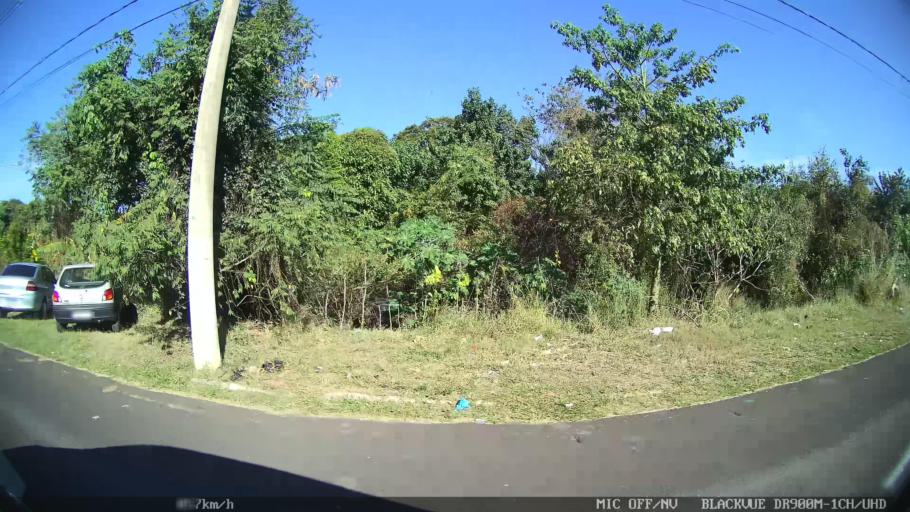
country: BR
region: Sao Paulo
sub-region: Franca
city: Franca
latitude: -20.4857
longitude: -47.4236
